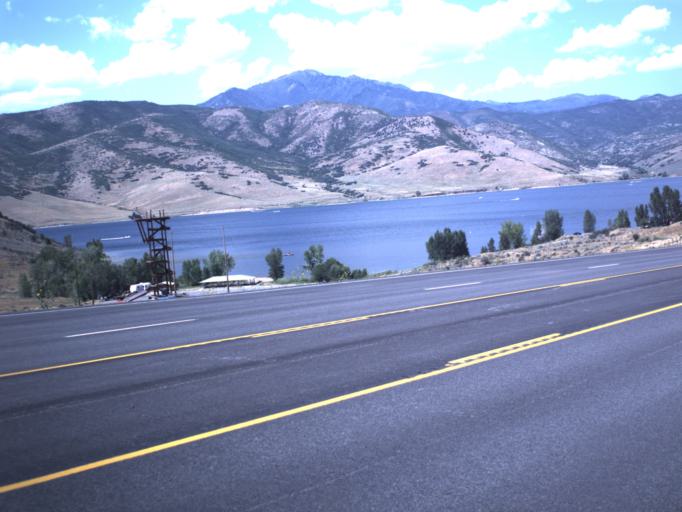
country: US
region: Utah
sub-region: Wasatch County
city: Midway
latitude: 40.4214
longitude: -111.4895
